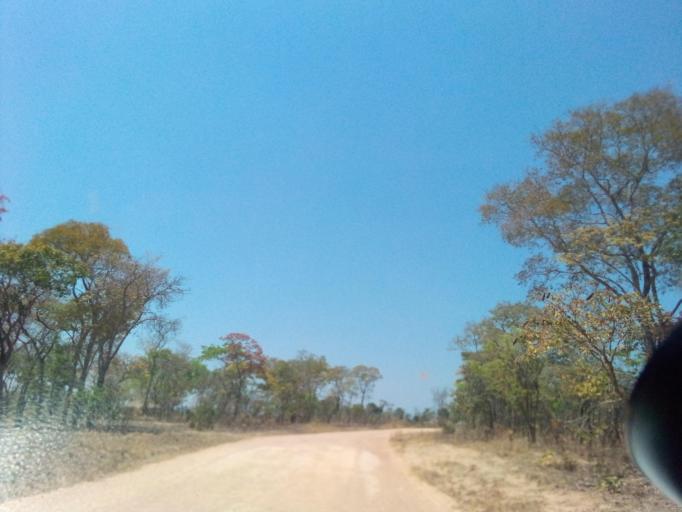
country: ZM
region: Northern
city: Mpika
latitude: -12.2264
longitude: 30.6557
